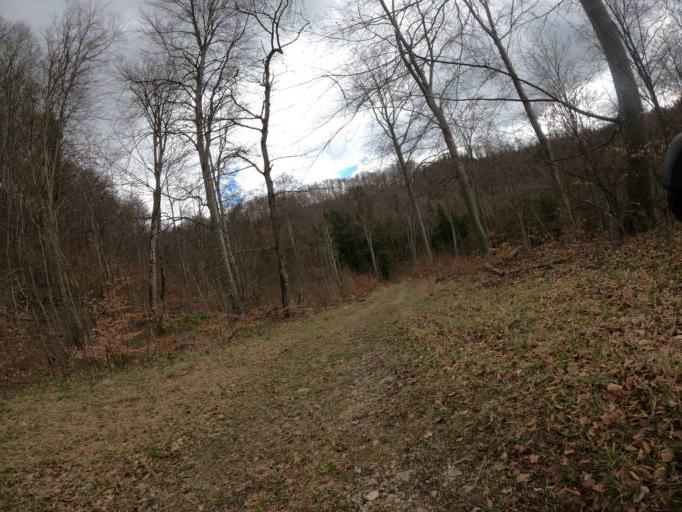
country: DE
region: Baden-Wuerttemberg
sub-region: Tuebingen Region
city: Jungingen
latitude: 48.3591
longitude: 9.0576
